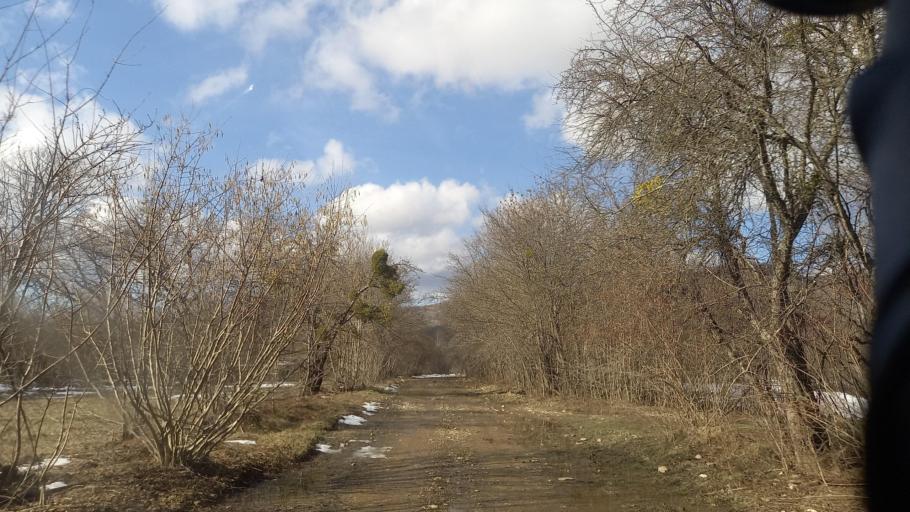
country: RU
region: Krasnodarskiy
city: Smolenskaya
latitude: 44.5963
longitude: 38.8823
